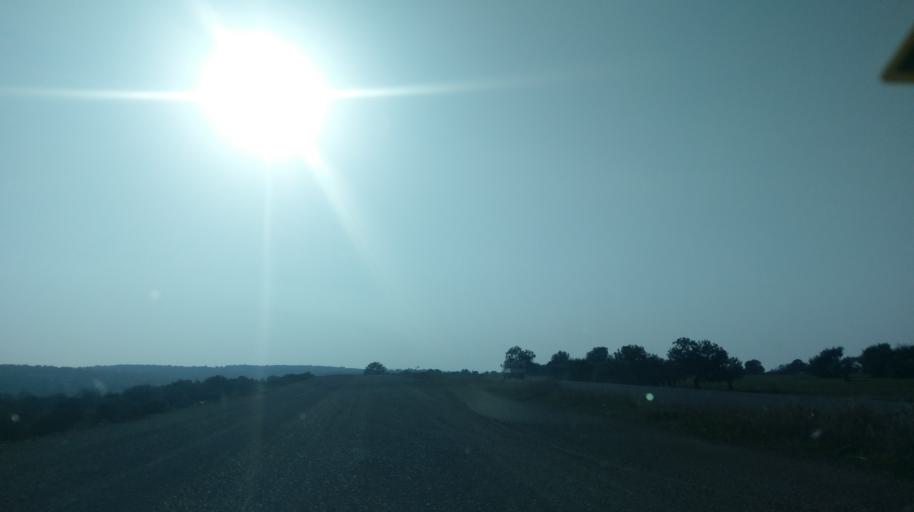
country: CY
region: Ammochostos
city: Leonarisso
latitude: 35.5137
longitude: 34.1555
